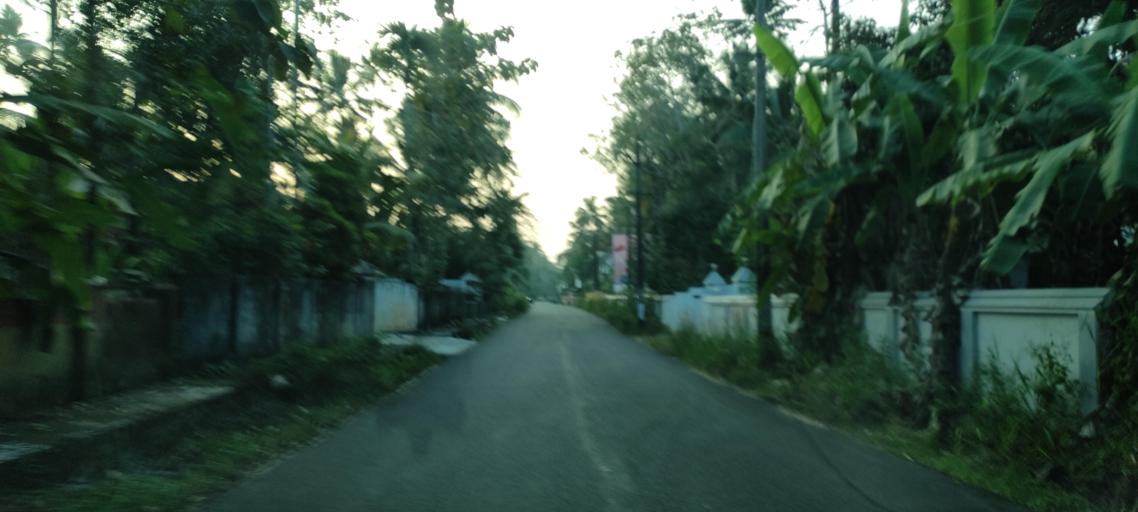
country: IN
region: Kerala
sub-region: Alappuzha
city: Kayankulam
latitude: 9.1352
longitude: 76.5319
